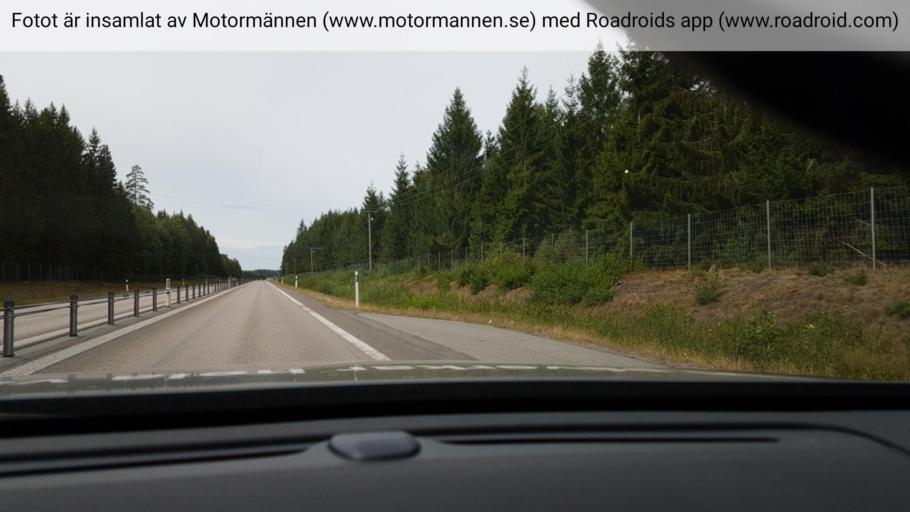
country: SE
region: Vaestra Goetaland
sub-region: Lidkopings Kommun
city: Vinninga
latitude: 58.3506
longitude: 13.3054
